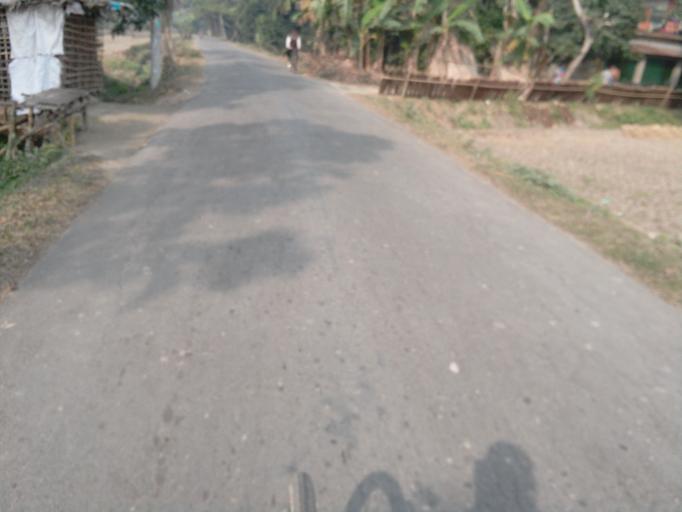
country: BD
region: Khulna
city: Kesabpur
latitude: 22.7502
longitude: 89.2401
